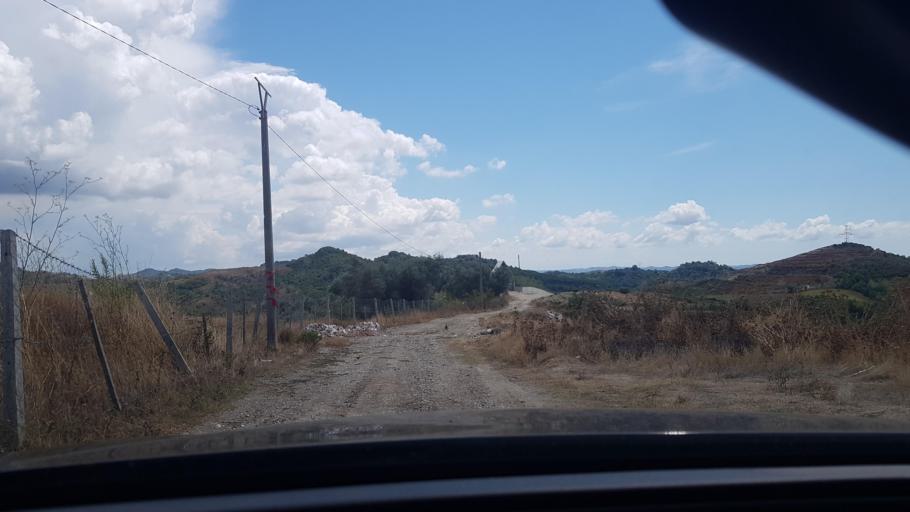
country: AL
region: Tirane
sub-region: Rrethi i Kavajes
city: Golem
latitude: 41.2820
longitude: 19.5456
